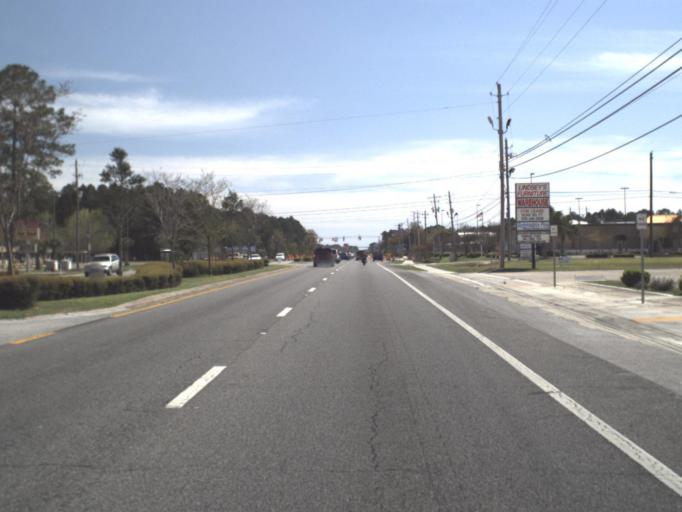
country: US
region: Florida
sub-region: Bay County
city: Hiland Park
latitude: 30.2051
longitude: -85.6498
